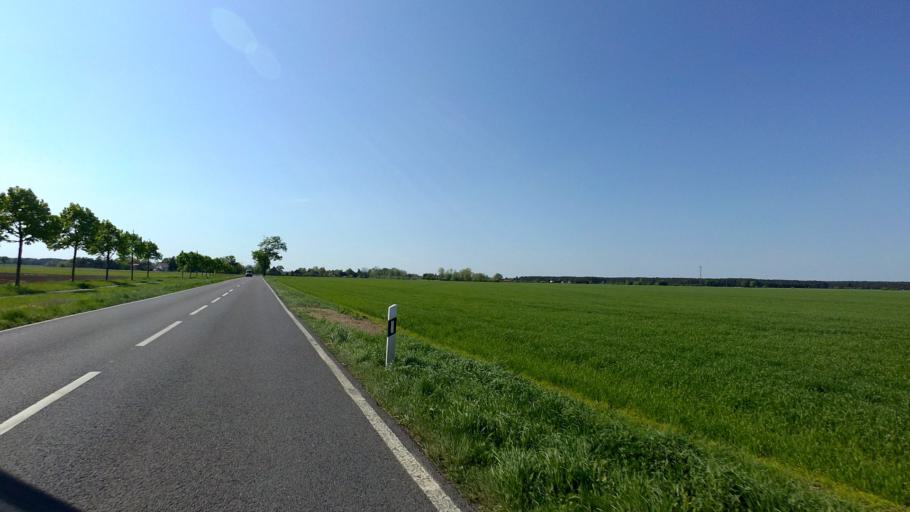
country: DE
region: Brandenburg
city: Schlepzig
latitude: 52.0543
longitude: 13.9756
